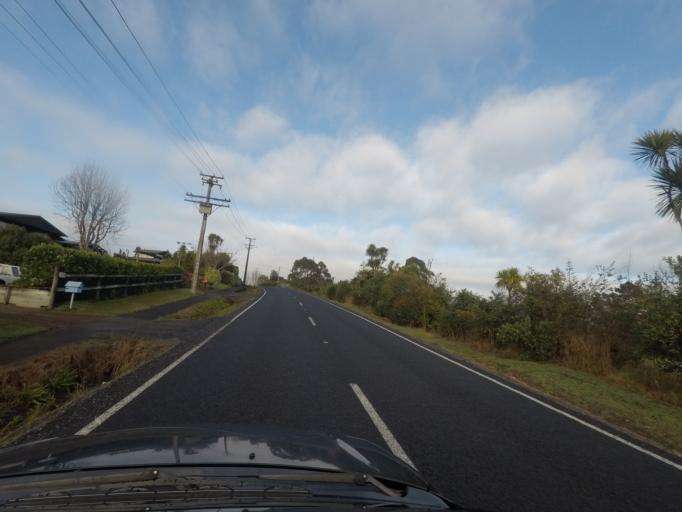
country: NZ
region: Auckland
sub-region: Auckland
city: Waitakere
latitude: -36.9018
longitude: 174.6134
